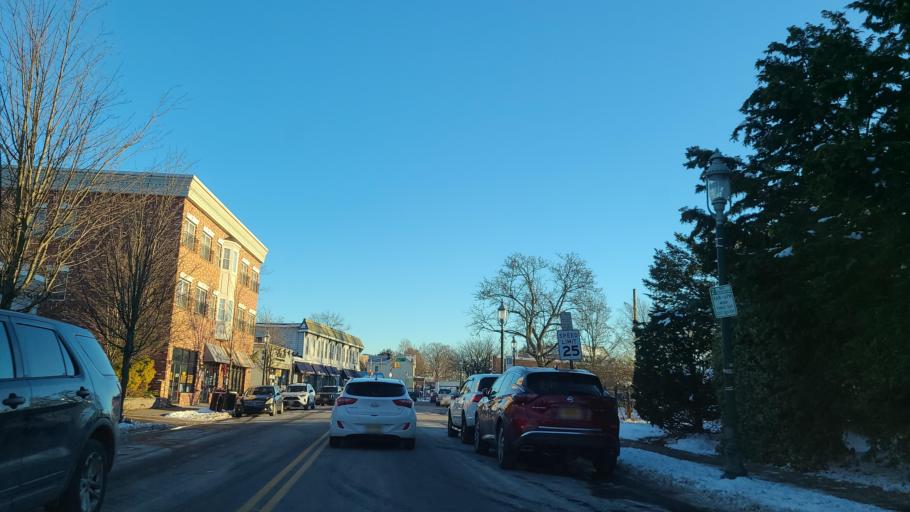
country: US
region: New Jersey
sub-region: Essex County
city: South Orange
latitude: 40.7412
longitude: -74.2535
